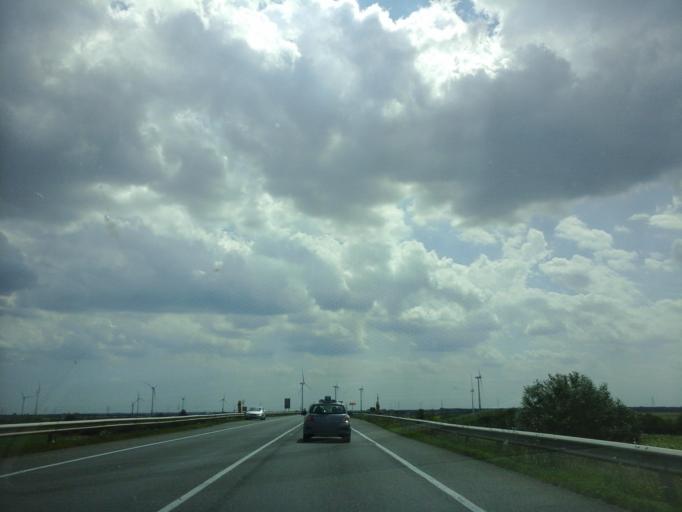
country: HU
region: Gyor-Moson-Sopron
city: Mosonmagyarovar
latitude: 47.8979
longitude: 17.1822
